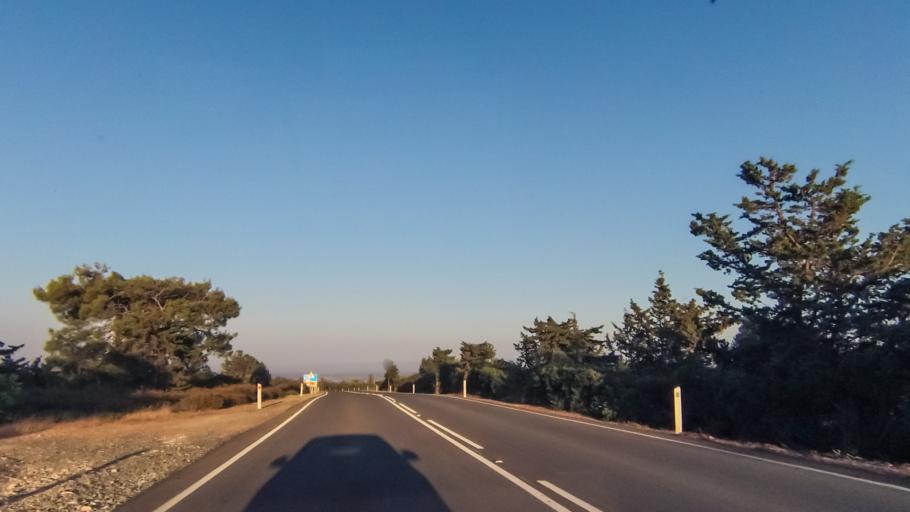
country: CY
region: Limassol
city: Sotira
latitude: 34.6708
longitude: 32.8593
